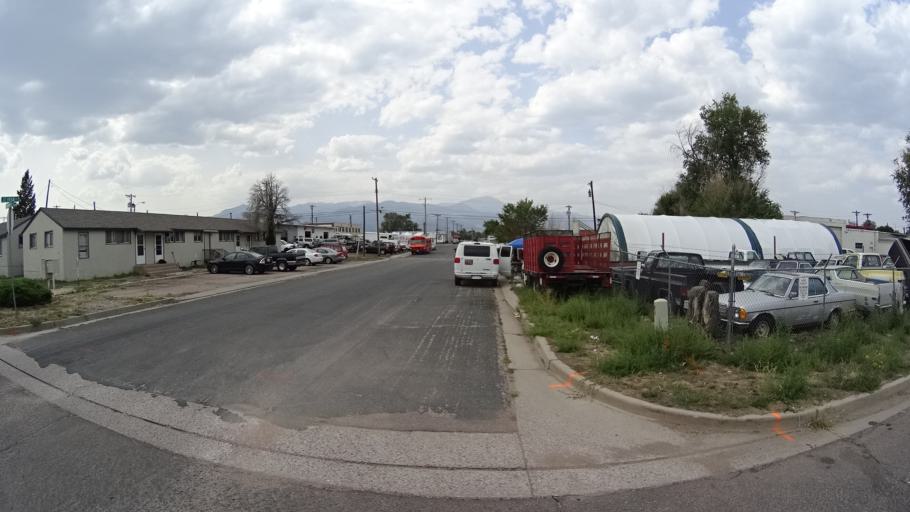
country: US
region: Colorado
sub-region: El Paso County
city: Colorado Springs
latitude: 38.8387
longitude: -104.7718
